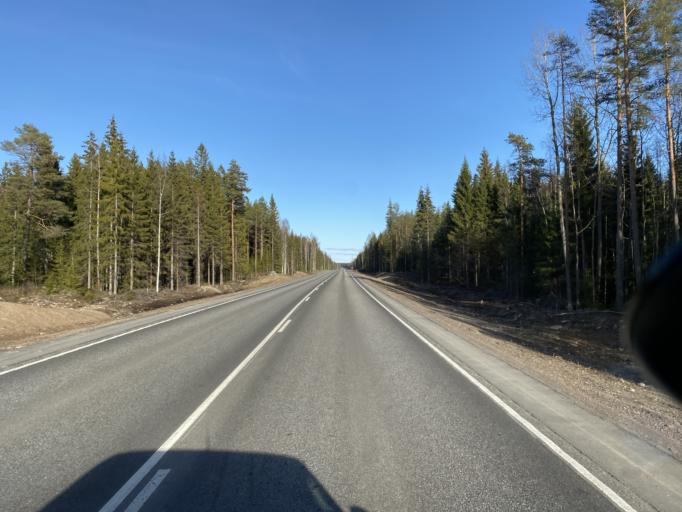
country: FI
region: Satakunta
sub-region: Pori
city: Huittinen
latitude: 61.1731
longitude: 22.5187
